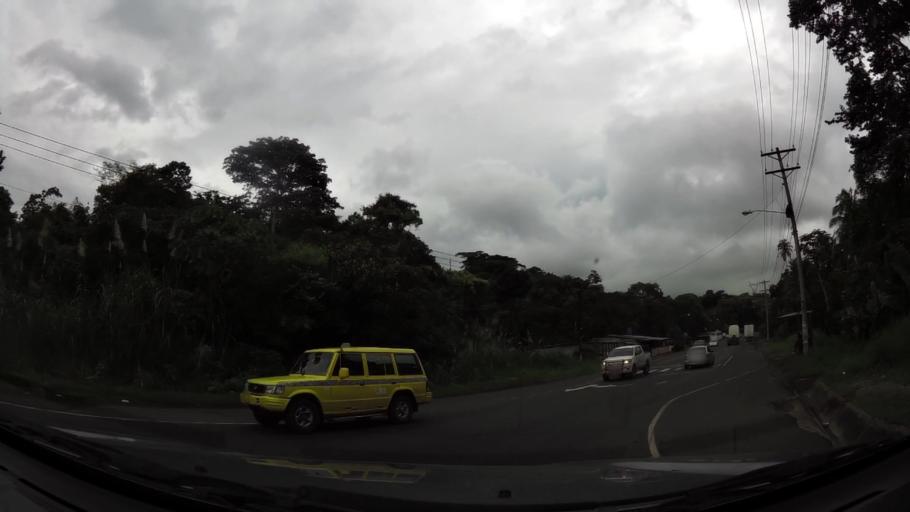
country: PA
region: Panama
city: Chilibre
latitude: 9.1859
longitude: -79.6159
